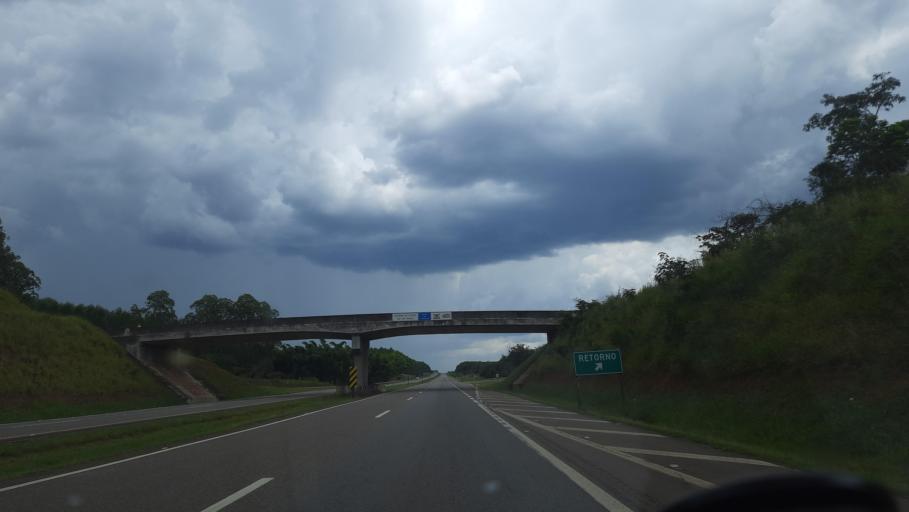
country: BR
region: Sao Paulo
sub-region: Casa Branca
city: Casa Branca
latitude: -21.8566
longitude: -47.0632
